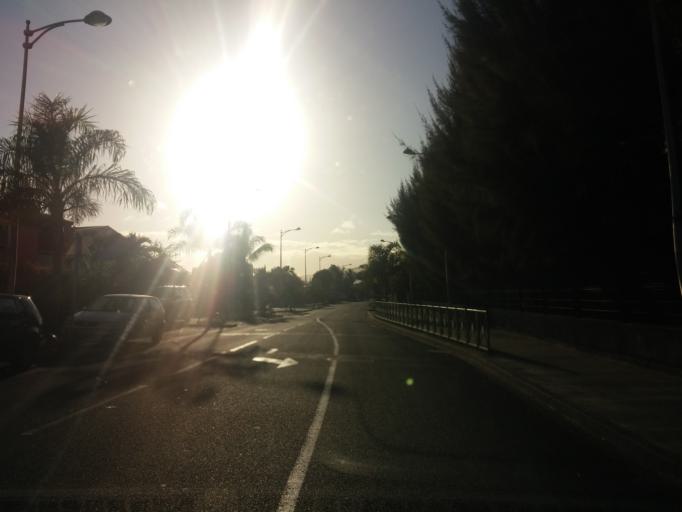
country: RE
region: Reunion
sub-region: Reunion
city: Le Port
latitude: -20.9356
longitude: 55.2970
